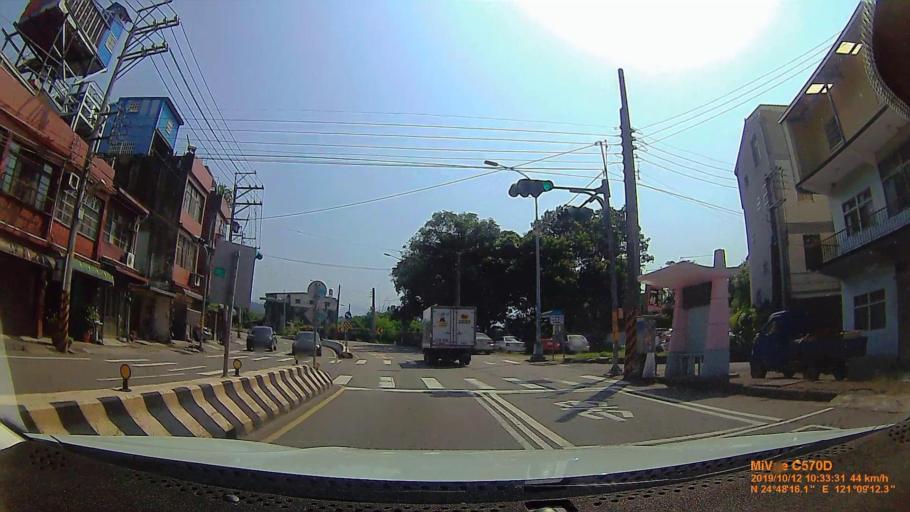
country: TW
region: Taiwan
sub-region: Hsinchu
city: Zhubei
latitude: 24.8044
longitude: 121.1535
